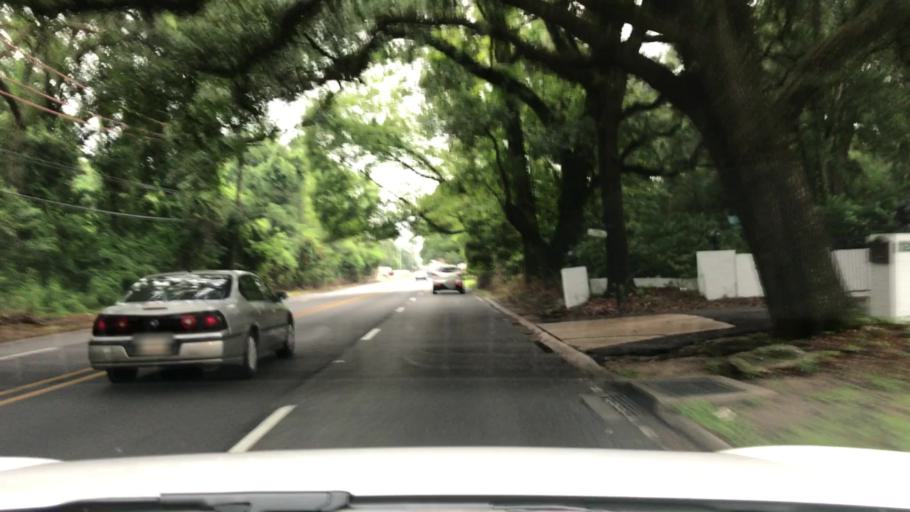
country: US
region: Louisiana
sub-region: East Baton Rouge Parish
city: Baton Rouge
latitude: 30.4568
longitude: -91.1392
